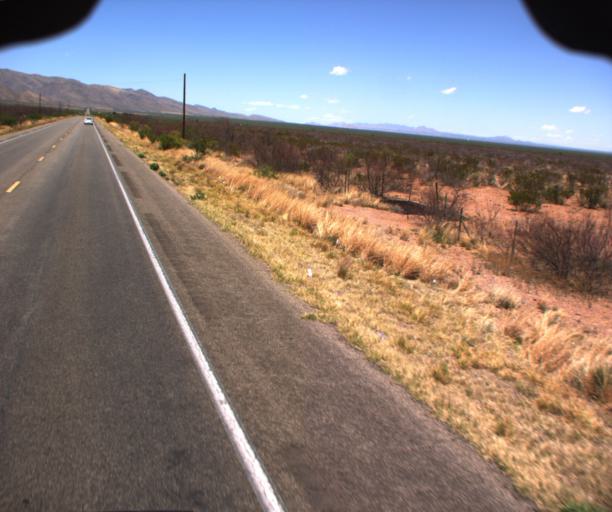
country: US
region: Arizona
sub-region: Cochise County
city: Bisbee
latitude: 31.3938
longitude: -109.7678
